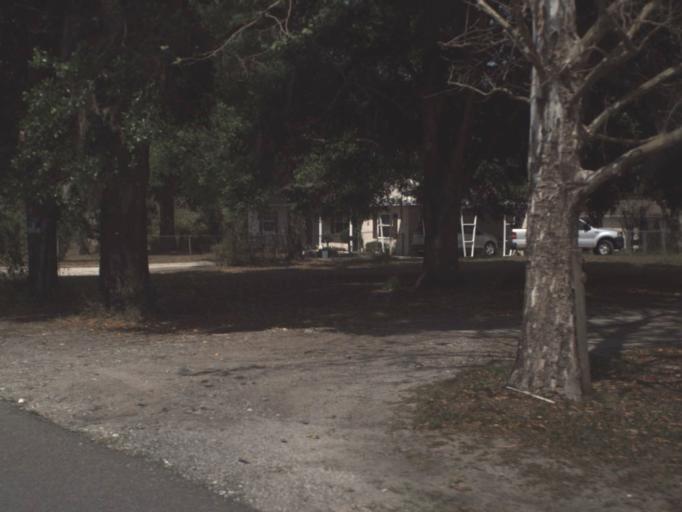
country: US
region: Florida
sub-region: Lake County
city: Groveland
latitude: 28.5758
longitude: -81.8556
